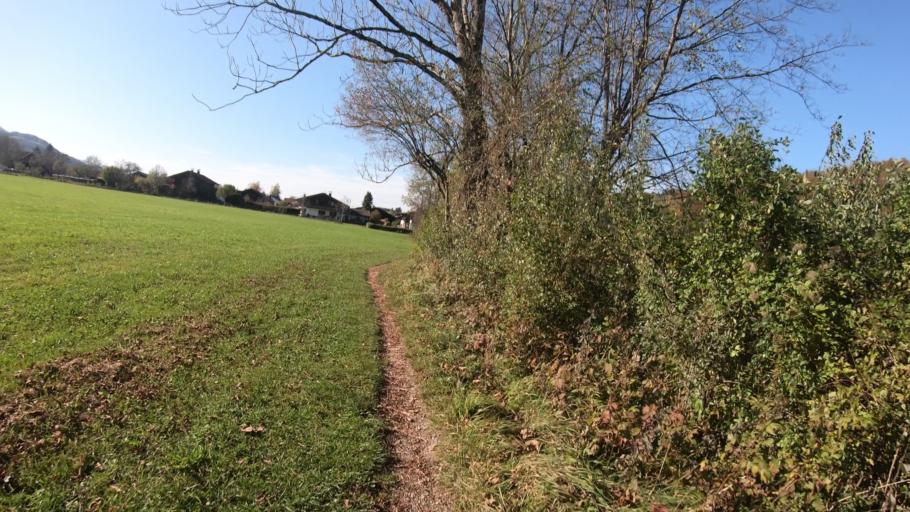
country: DE
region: Bavaria
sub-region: Upper Bavaria
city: Bergen
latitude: 47.8055
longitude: 12.5971
